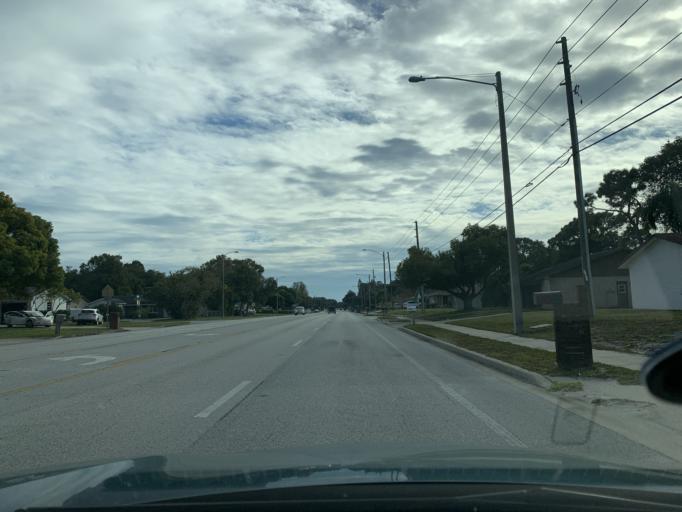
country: US
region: Florida
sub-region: Pinellas County
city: Kenneth City
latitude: 27.8274
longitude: -82.7368
